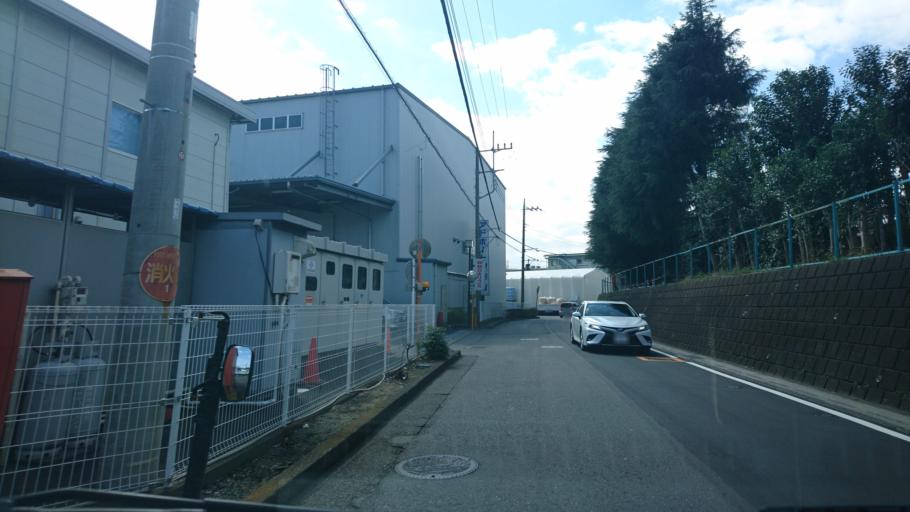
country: JP
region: Kanagawa
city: Zama
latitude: 35.5308
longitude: 139.3282
